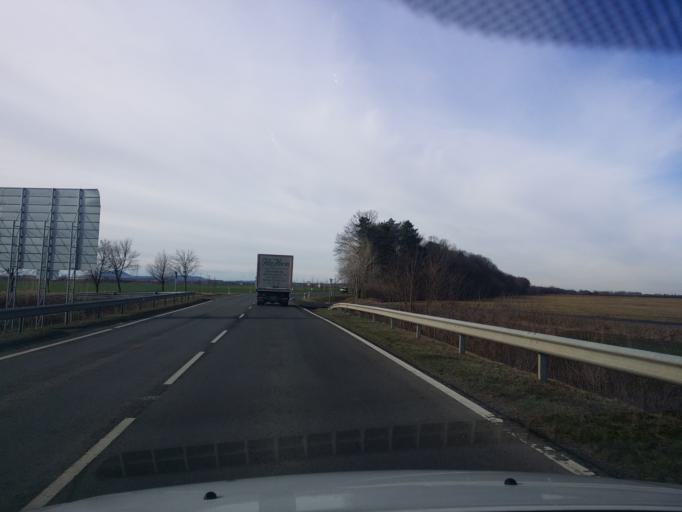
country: HU
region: Baranya
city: Lanycsok
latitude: 45.9908
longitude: 18.5759
